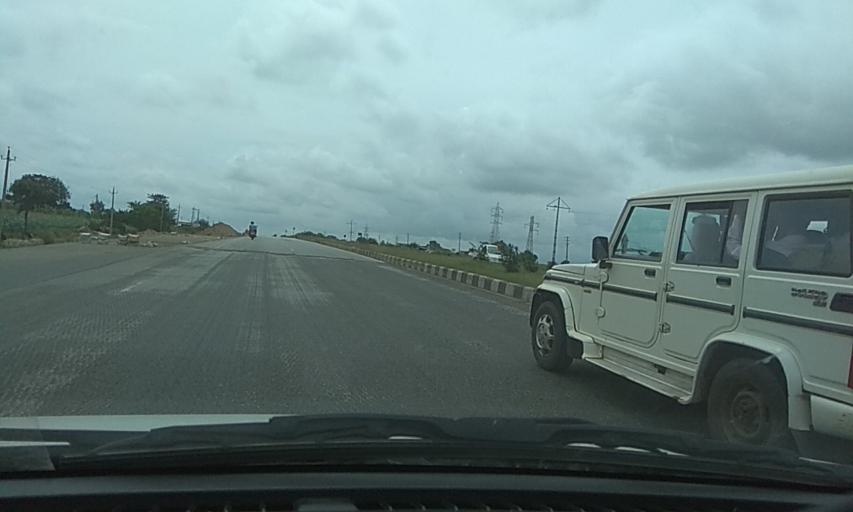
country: IN
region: Karnataka
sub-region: Davanagere
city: Mayakonda
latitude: 14.3307
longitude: 76.2205
